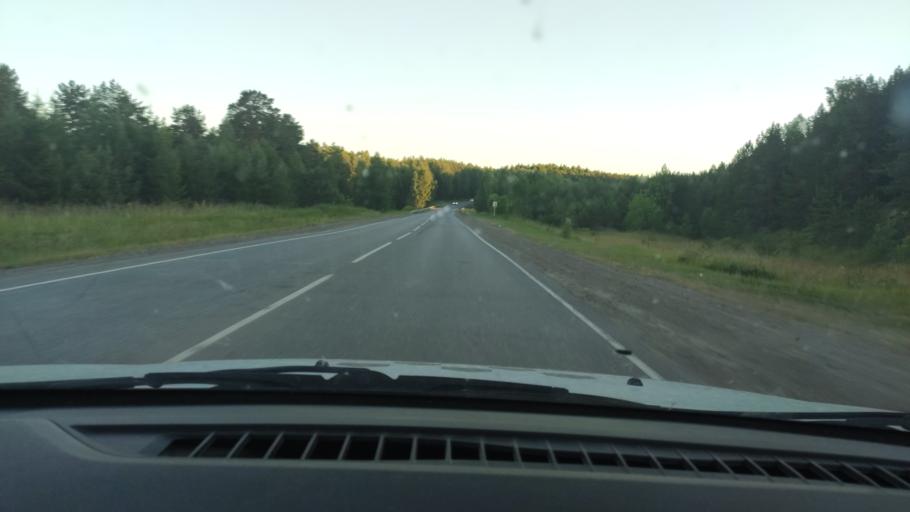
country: RU
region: Perm
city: Kungur
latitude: 57.4164
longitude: 56.9153
